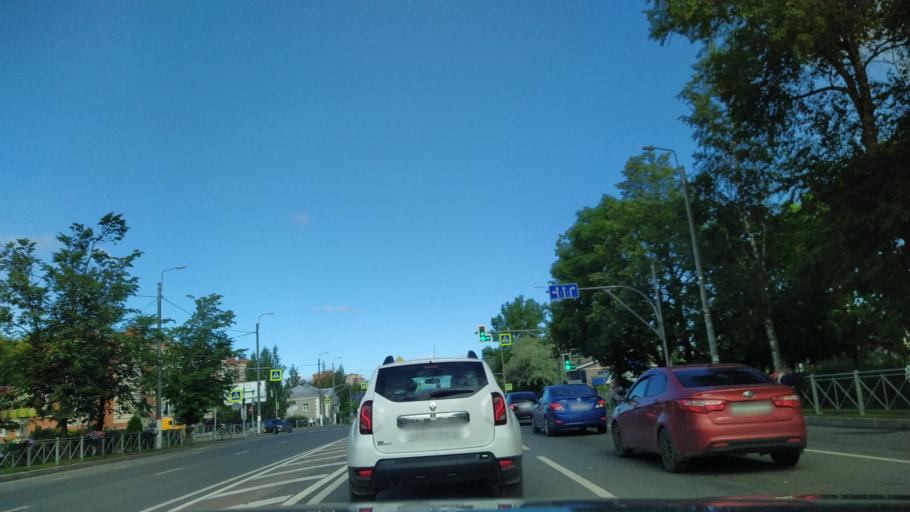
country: RU
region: Leningrad
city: Tosno
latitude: 59.5446
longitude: 30.8705
